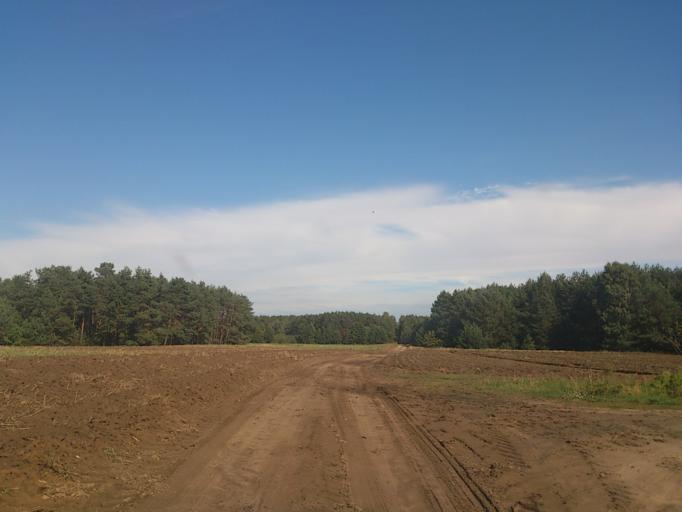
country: PL
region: Kujawsko-Pomorskie
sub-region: Powiat golubsko-dobrzynski
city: Golub-Dobrzyn
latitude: 53.1289
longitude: 19.1262
